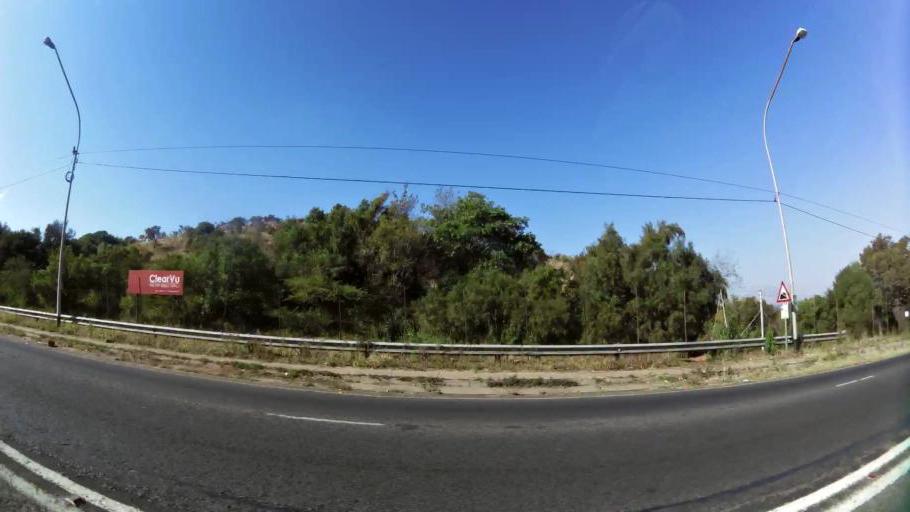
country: ZA
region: Gauteng
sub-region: City of Tshwane Metropolitan Municipality
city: Pretoria
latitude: -25.6923
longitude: 28.1985
